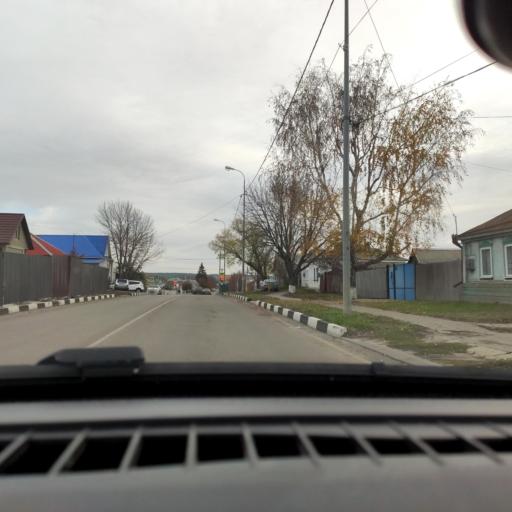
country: RU
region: Belgorod
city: Alekseyevka
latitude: 50.6297
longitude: 38.7032
